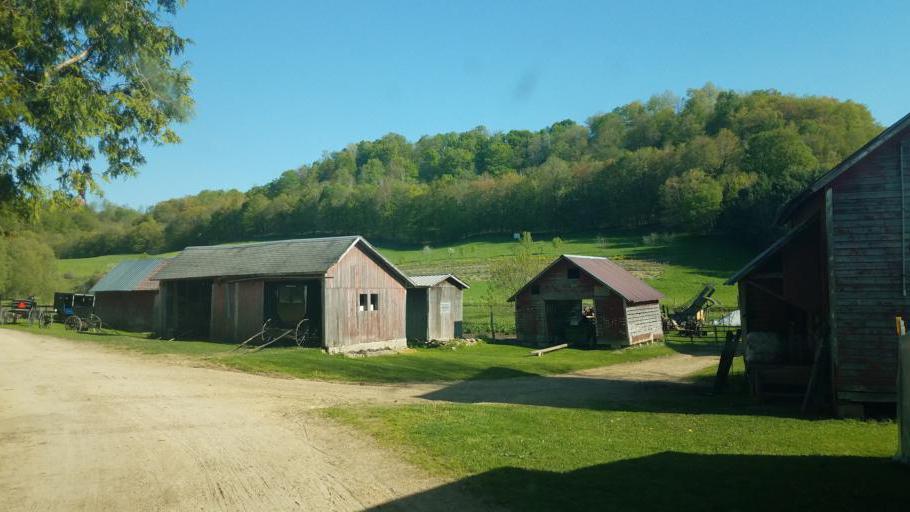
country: US
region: Wisconsin
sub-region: Vernon County
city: Hillsboro
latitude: 43.6226
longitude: -90.4844
